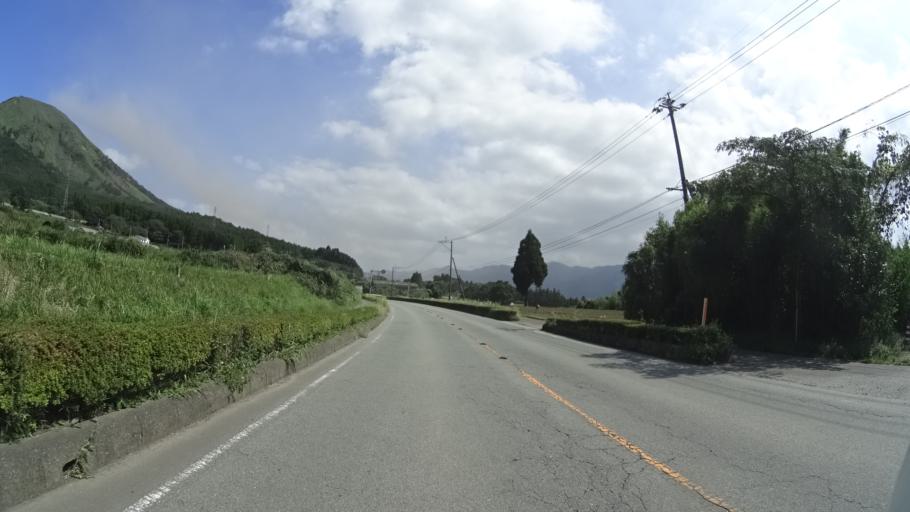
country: JP
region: Kumamoto
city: Aso
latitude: 32.8515
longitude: 131.0233
